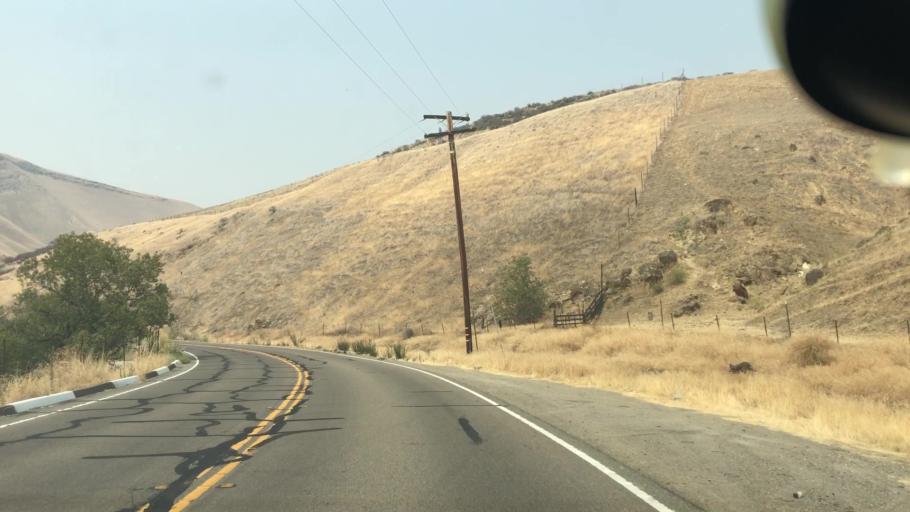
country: US
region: California
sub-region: San Joaquin County
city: Tracy
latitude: 37.6529
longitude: -121.4873
